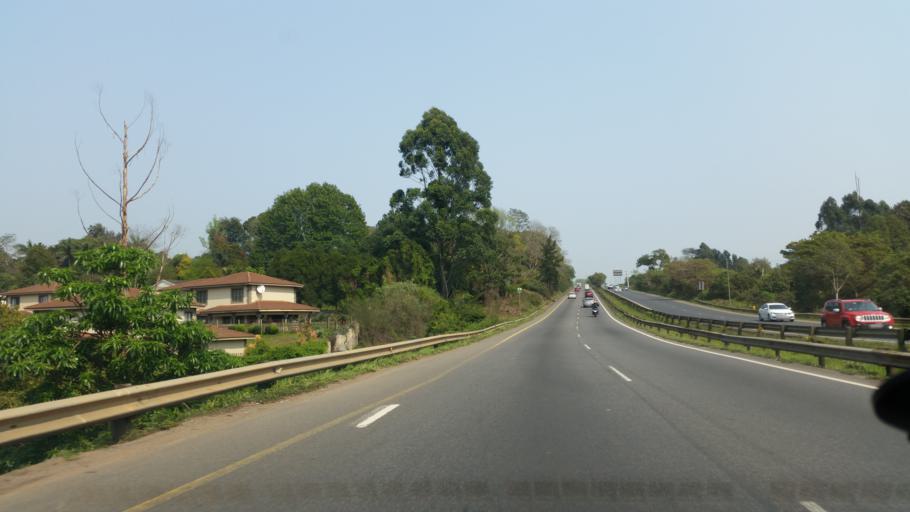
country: ZA
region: KwaZulu-Natal
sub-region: eThekwini Metropolitan Municipality
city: Mpumalanga
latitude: -29.7941
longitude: 30.7968
